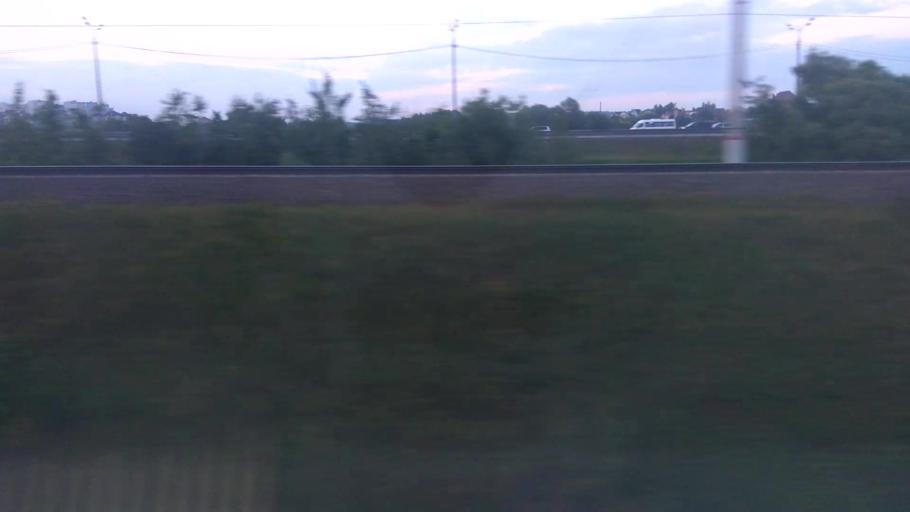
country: RU
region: Moskovskaya
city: Vidnoye
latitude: 55.5191
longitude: 37.7058
